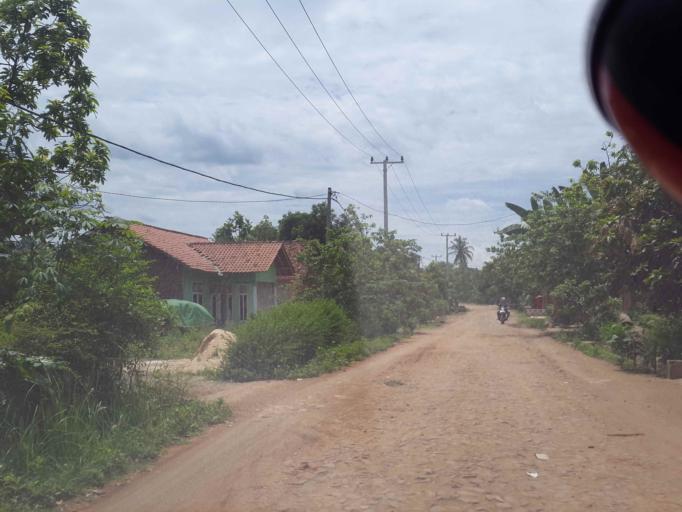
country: ID
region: Lampung
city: Natar
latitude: -5.3229
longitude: 105.1936
